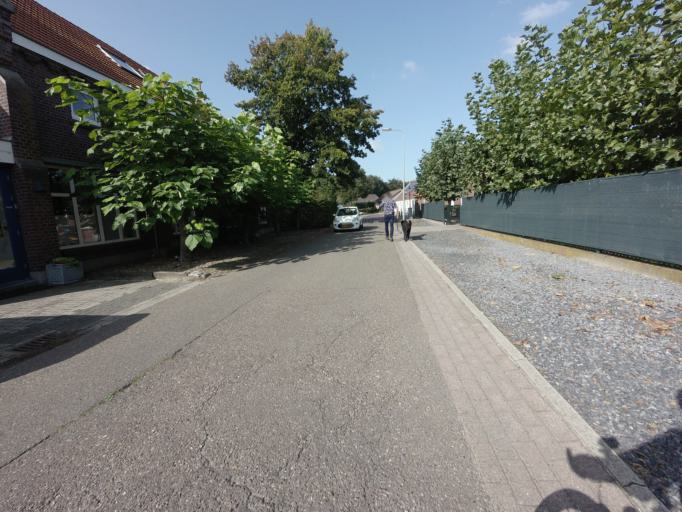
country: NL
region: Limburg
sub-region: Gemeente Roerdalen
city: Herkenbosch
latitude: 51.1922
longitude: 6.0493
